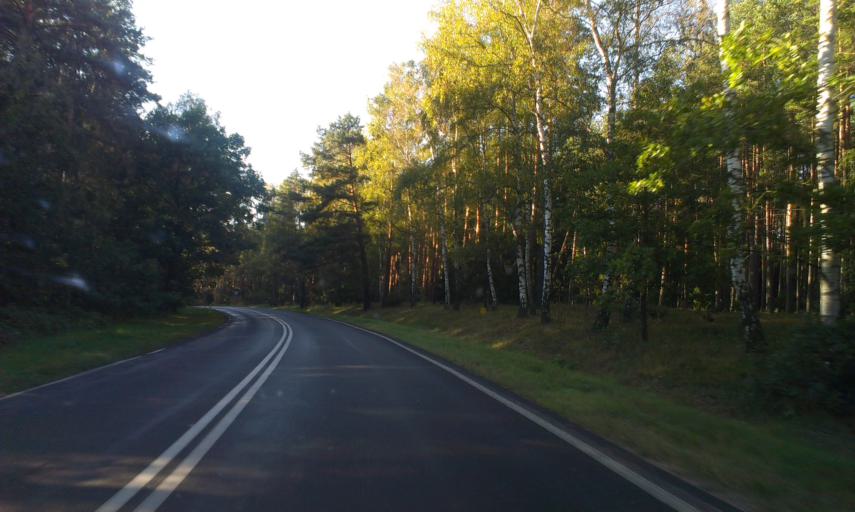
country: PL
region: Kujawsko-Pomorskie
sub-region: Powiat tucholski
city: Tuchola
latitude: 53.5506
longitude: 17.9247
